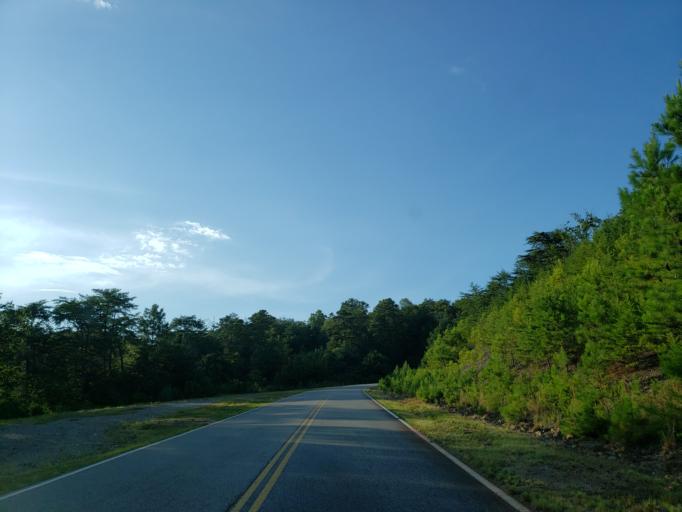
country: US
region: Georgia
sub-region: Cherokee County
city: Canton
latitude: 34.2301
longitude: -84.5737
